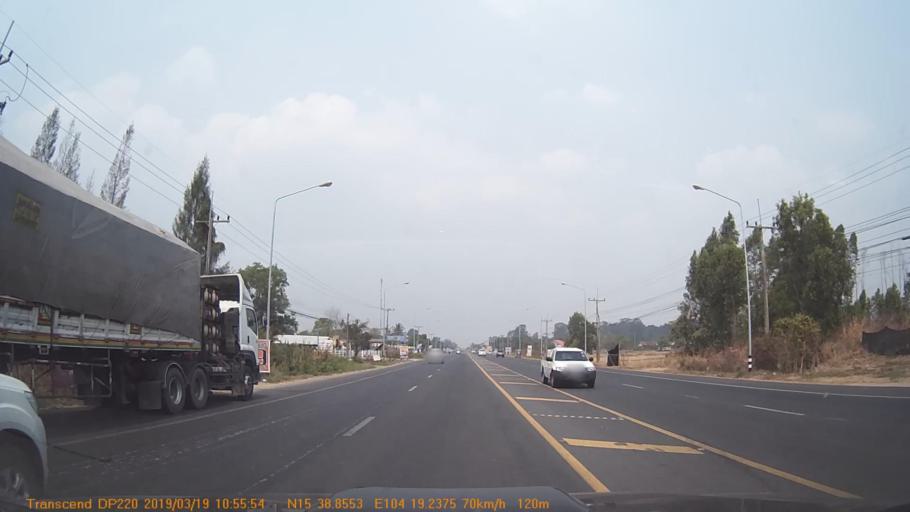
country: TH
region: Yasothon
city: Kham Khuean Kaeo
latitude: 15.6477
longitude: 104.3204
